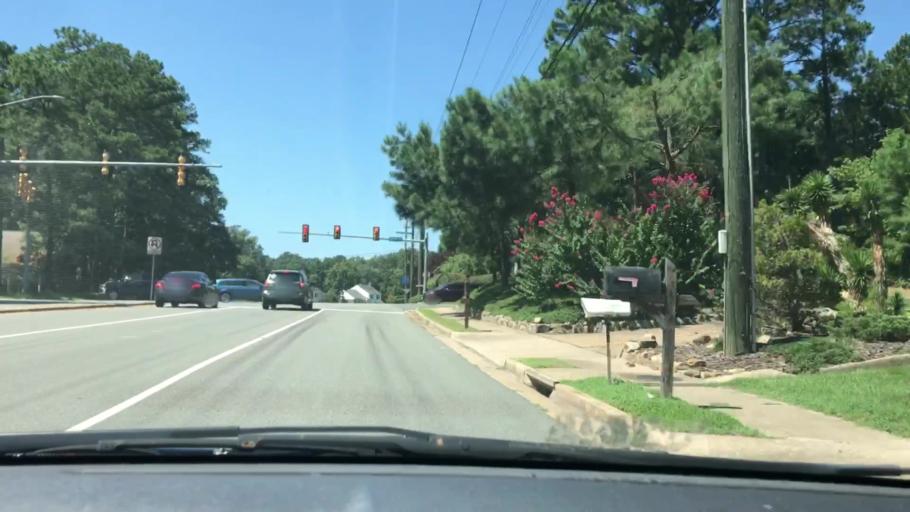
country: US
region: Virginia
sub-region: Henrico County
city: Short Pump
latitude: 37.6074
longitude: -77.6061
